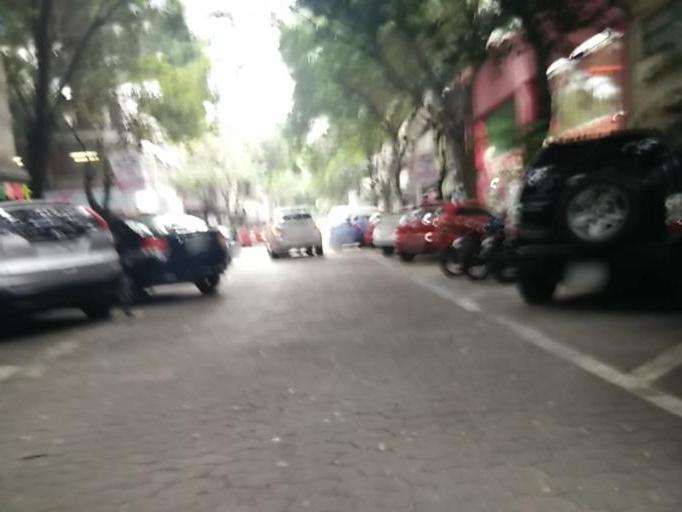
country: MX
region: Mexico City
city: Cuauhtemoc
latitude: 19.4269
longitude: -99.1659
